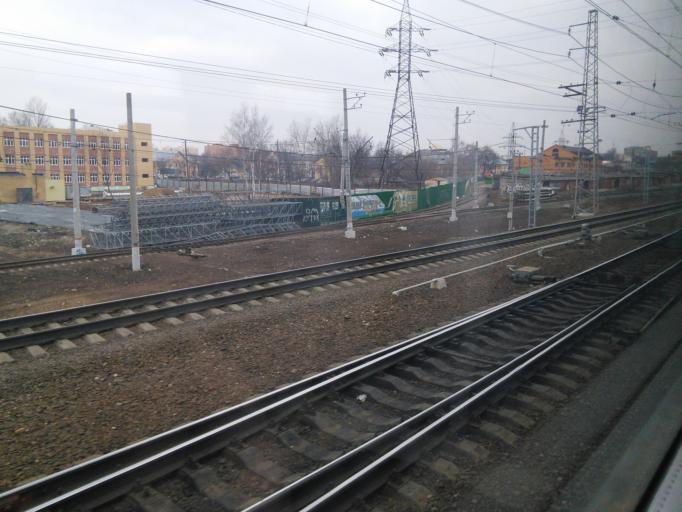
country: RU
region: Moskovskaya
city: Domodedovo
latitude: 55.4337
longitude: 37.7774
